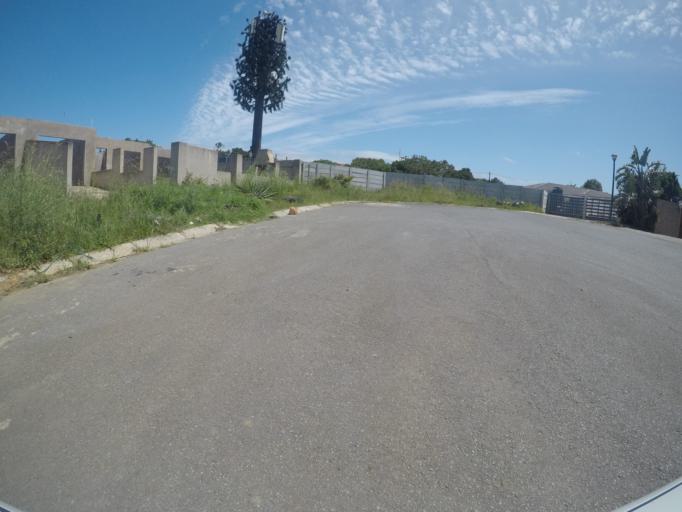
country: ZA
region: Eastern Cape
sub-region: Buffalo City Metropolitan Municipality
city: East London
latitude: -32.9416
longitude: 27.9966
